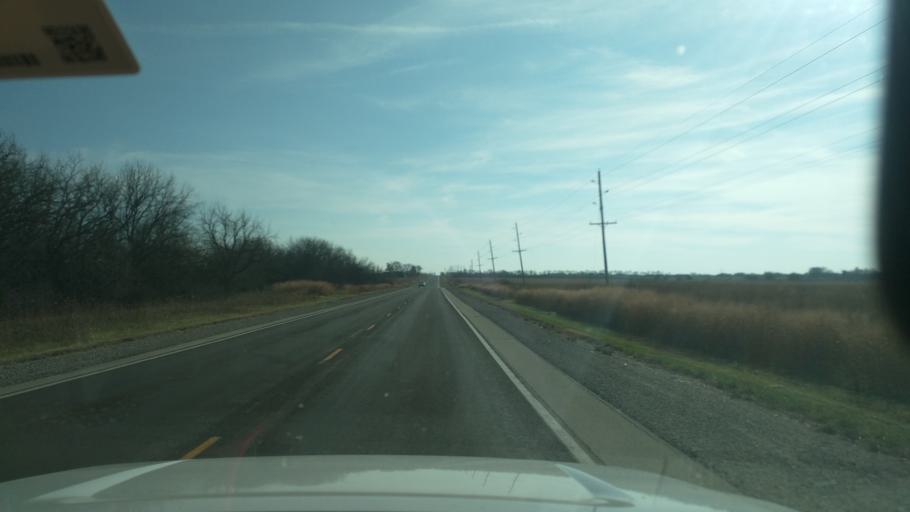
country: US
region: Kansas
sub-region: Lyon County
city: Emporia
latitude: 38.3070
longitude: -96.1804
